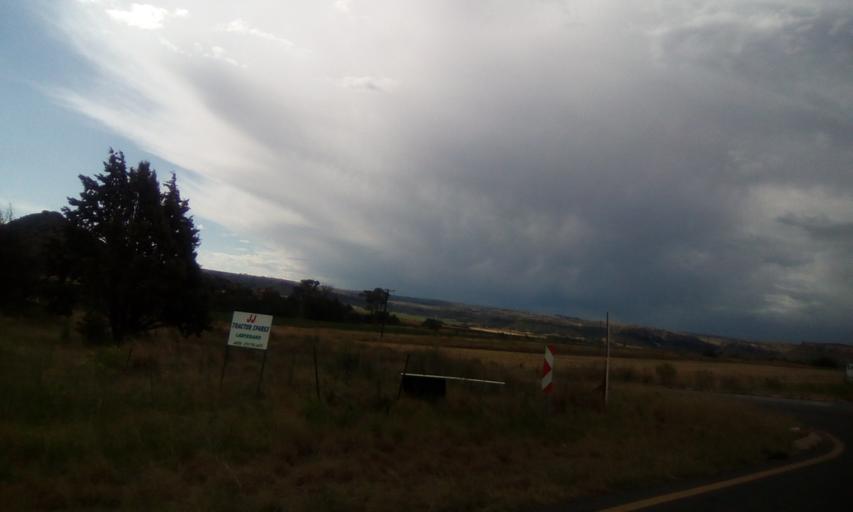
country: ZA
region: Orange Free State
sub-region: Thabo Mofutsanyana District Municipality
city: Ladybrand
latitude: -29.2551
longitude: 27.4331
